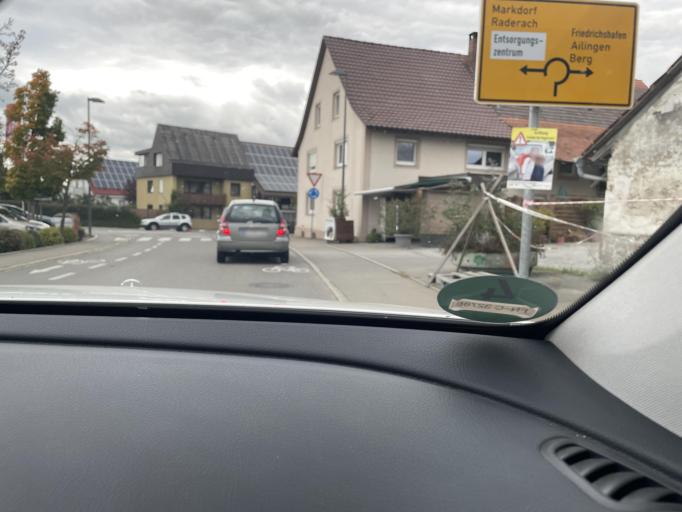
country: DE
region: Baden-Wuerttemberg
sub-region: Tuebingen Region
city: Oberteuringen
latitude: 47.6845
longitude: 9.4447
